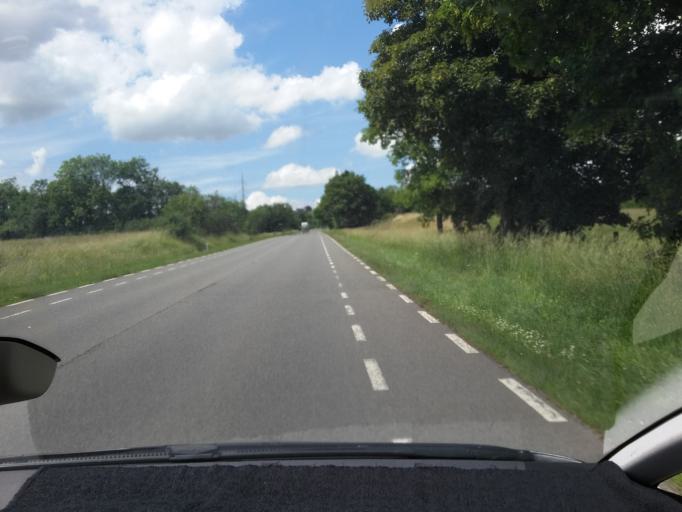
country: BE
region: Wallonia
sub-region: Province de Namur
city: Rochefort
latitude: 50.2214
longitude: 5.1808
